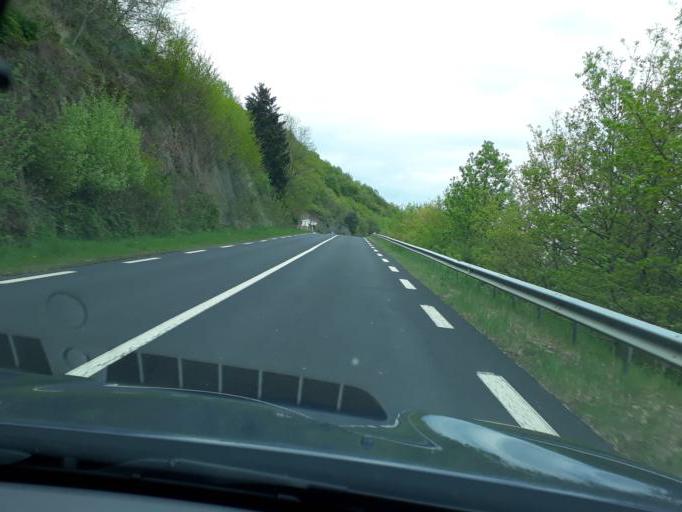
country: FR
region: Auvergne
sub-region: Departement du Cantal
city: Massiac
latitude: 45.2436
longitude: 3.2008
